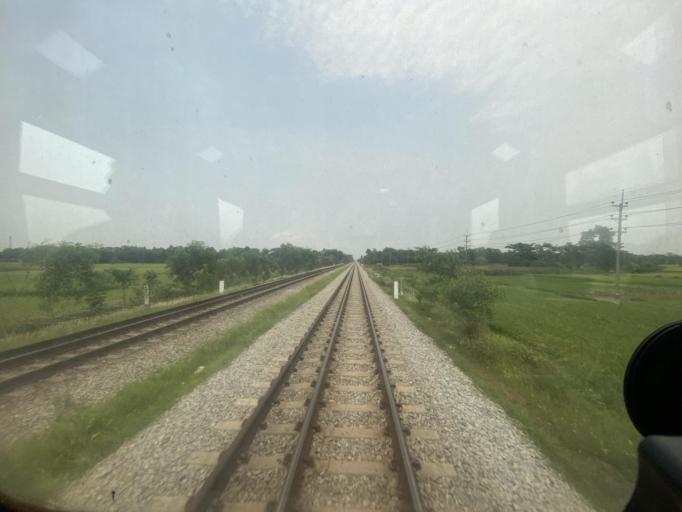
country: BD
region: Chittagong
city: Laksham
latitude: 23.3158
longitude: 91.1410
